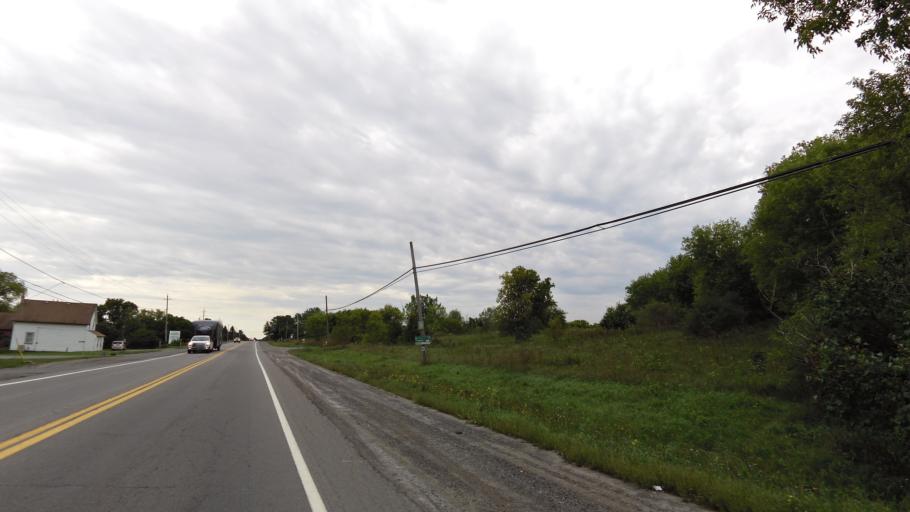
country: CA
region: Ontario
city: Ottawa
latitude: 45.2764
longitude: -75.5680
